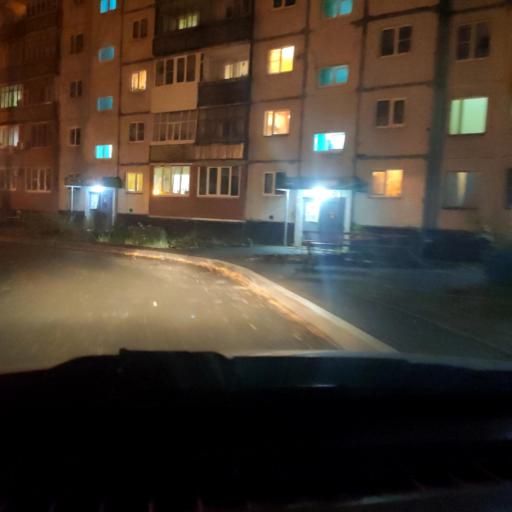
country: RU
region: Samara
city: Tol'yatti
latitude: 53.5106
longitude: 49.2667
